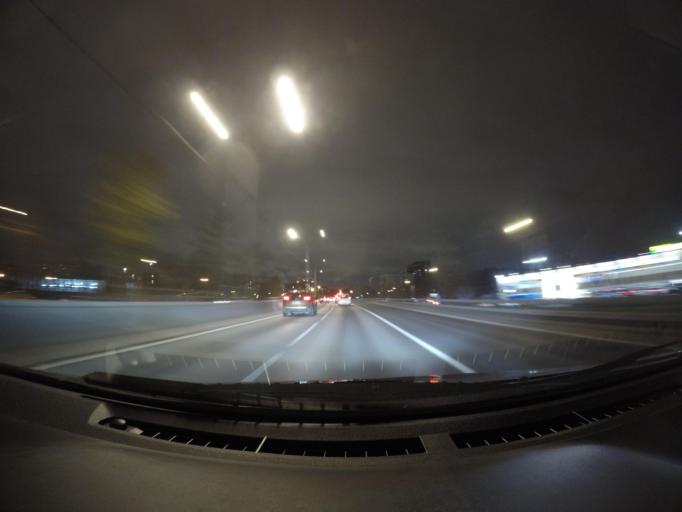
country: RU
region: Moscow
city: Kuz'minki
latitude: 55.7010
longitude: 37.7952
